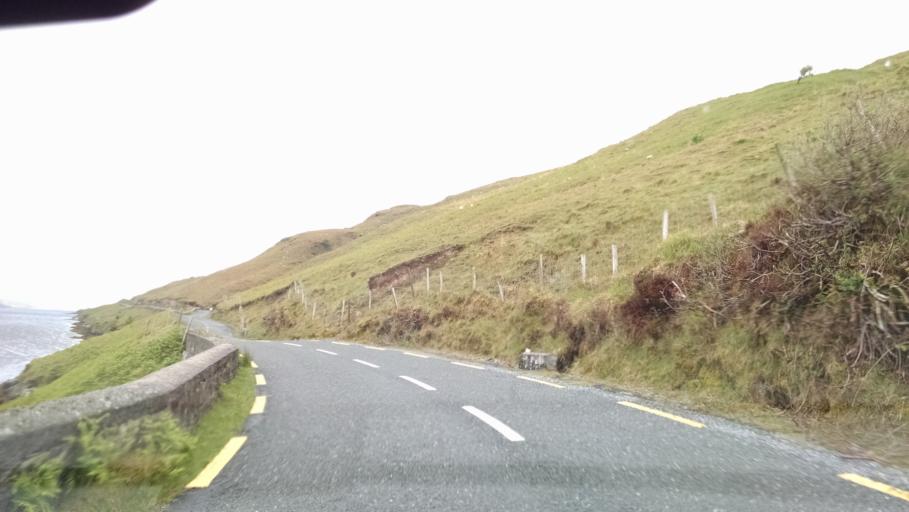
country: IE
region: Connaught
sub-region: Maigh Eo
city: Westport
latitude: 53.6052
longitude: -9.7119
